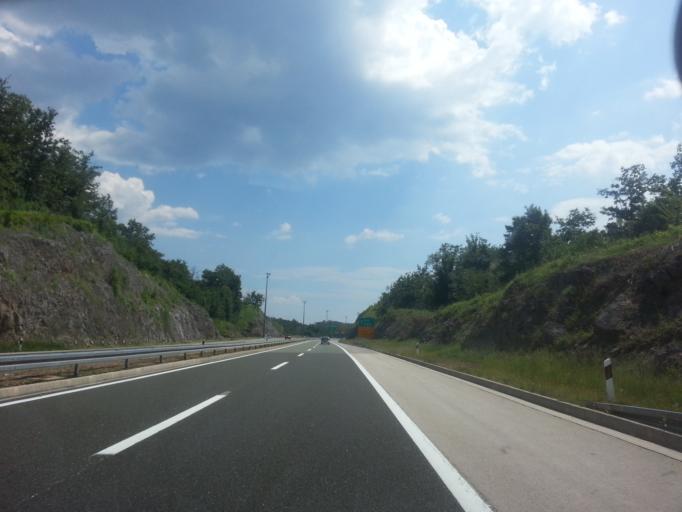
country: HR
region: Primorsko-Goranska
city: Matulji
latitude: 45.4015
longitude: 14.2998
